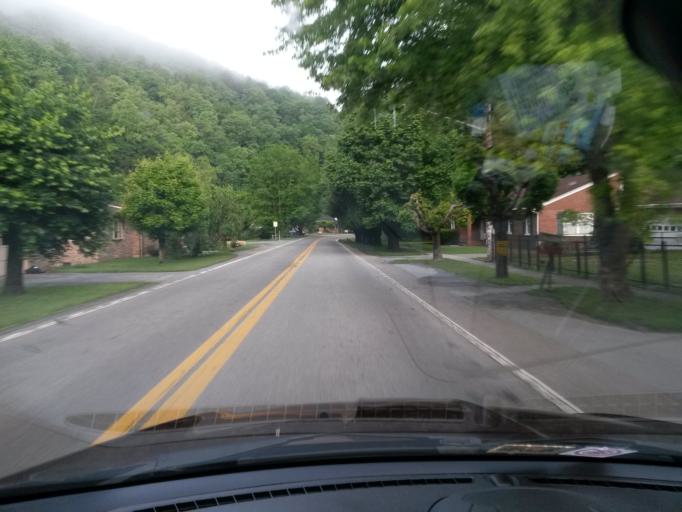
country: US
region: West Virginia
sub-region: McDowell County
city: Welch
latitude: 37.4479
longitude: -81.5596
